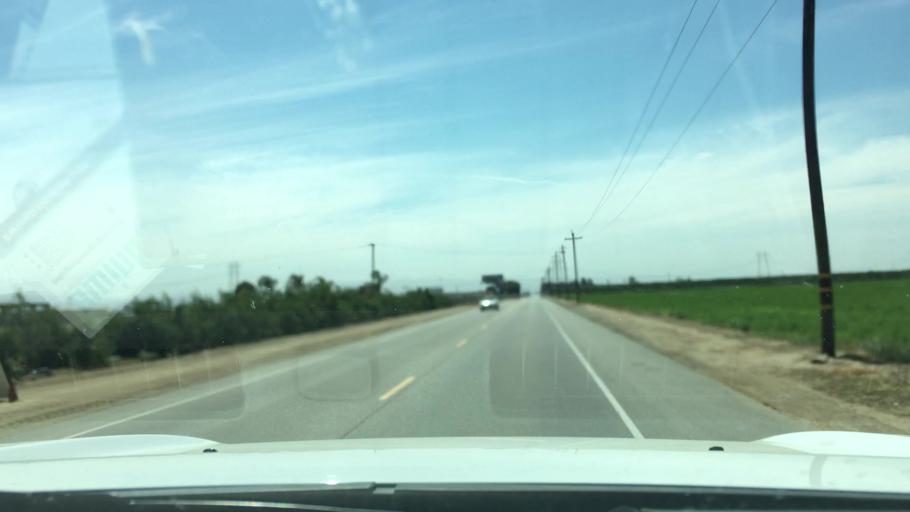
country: US
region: California
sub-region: Kern County
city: Rosedale
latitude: 35.3543
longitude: -119.2264
